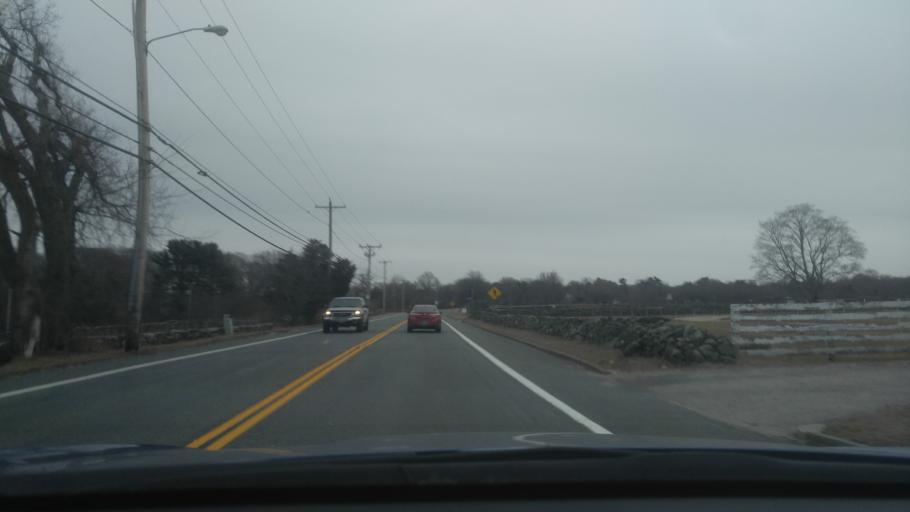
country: US
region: Rhode Island
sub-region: Newport County
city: Jamestown
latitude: 41.5124
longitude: -71.4223
